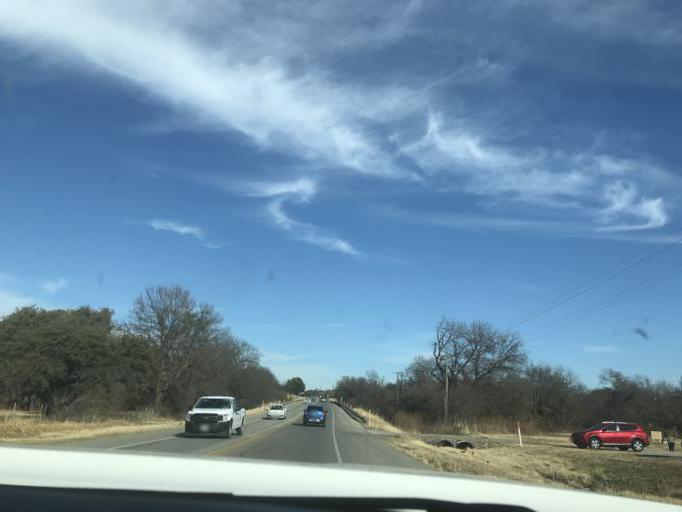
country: US
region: Texas
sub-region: Erath County
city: Stephenville
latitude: 32.2343
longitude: -98.2055
